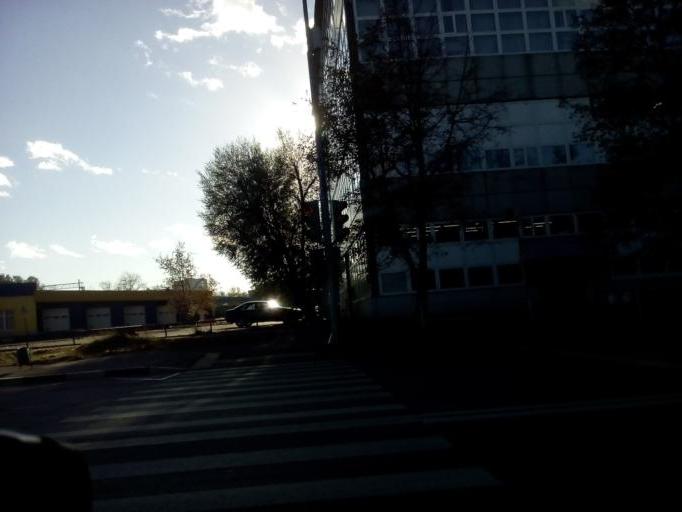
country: RU
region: Moscow
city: Zapadnoye Degunino
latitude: 55.8463
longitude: 37.5412
